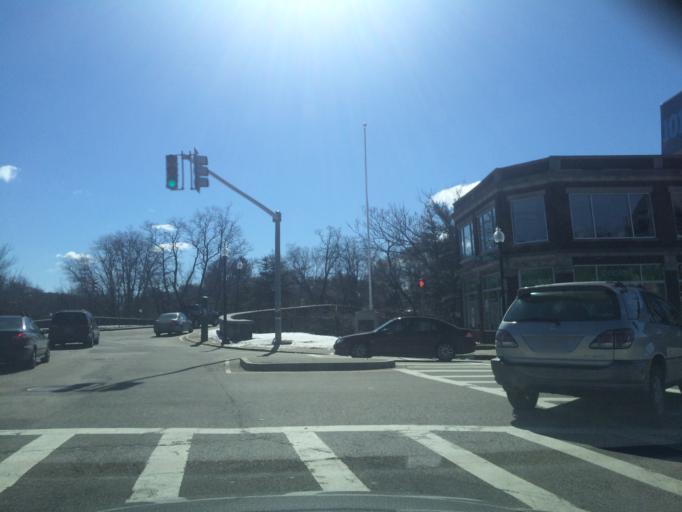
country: US
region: Massachusetts
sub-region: Norfolk County
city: Milton
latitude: 42.2676
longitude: -71.0945
